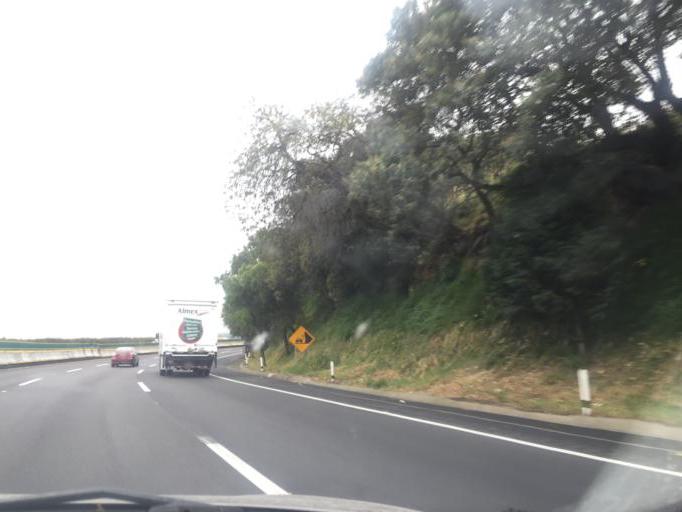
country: MX
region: Mexico City
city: Xochimilco
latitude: 19.2255
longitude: -99.1294
